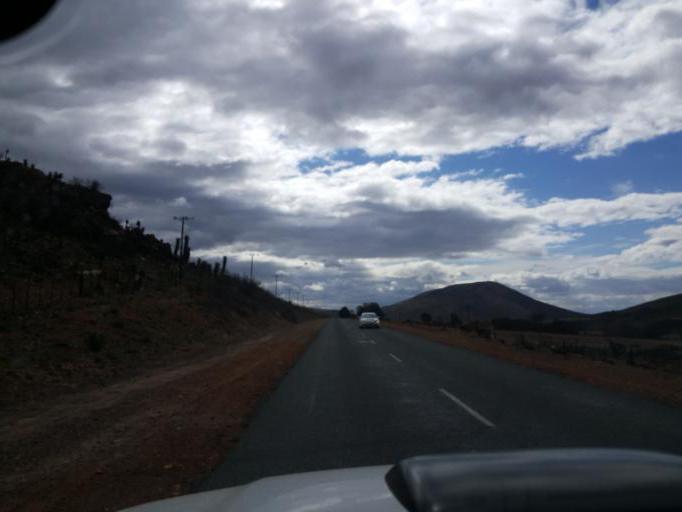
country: ZA
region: Western Cape
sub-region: Eden District Municipality
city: George
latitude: -33.8200
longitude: 22.3710
